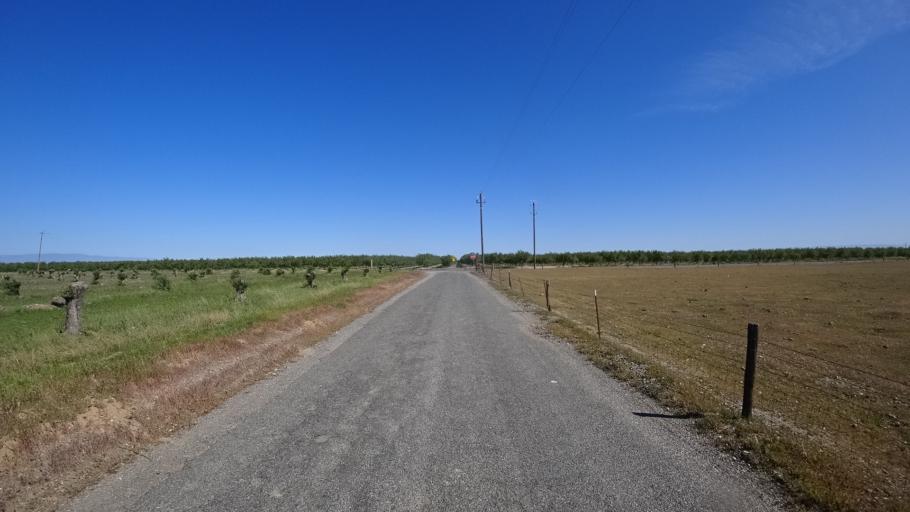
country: US
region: California
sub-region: Glenn County
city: Willows
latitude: 39.6232
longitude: -122.1564
